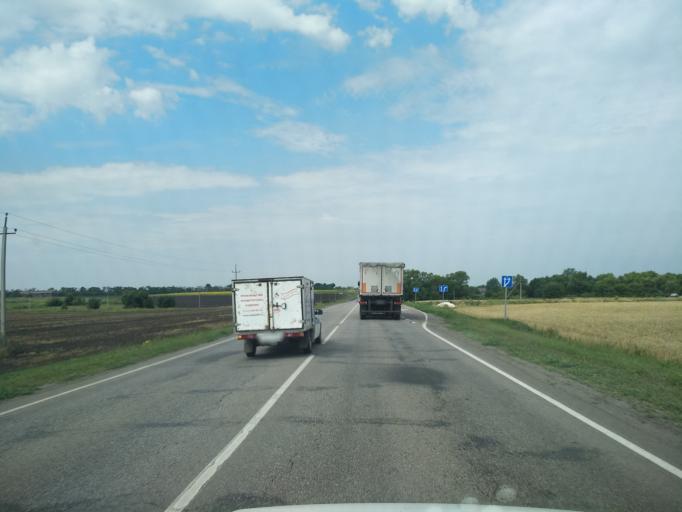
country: RU
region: Voronezj
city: Verkhnyaya Khava
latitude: 51.6779
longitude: 39.8646
